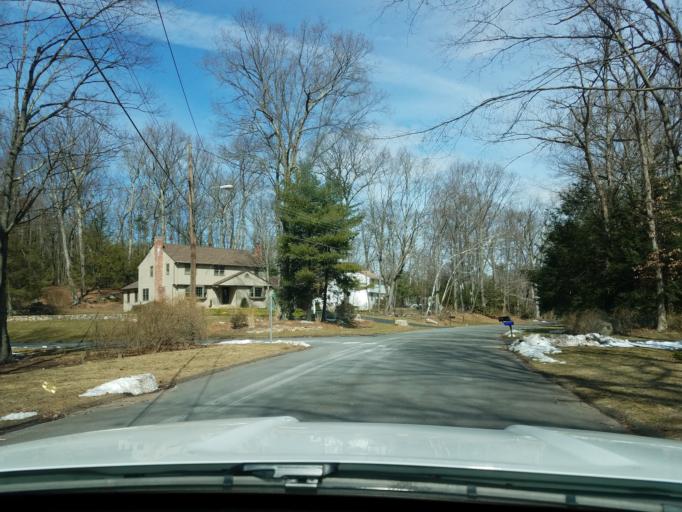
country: US
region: Connecticut
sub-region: Hartford County
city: Canton Valley
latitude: 41.7831
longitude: -72.8748
